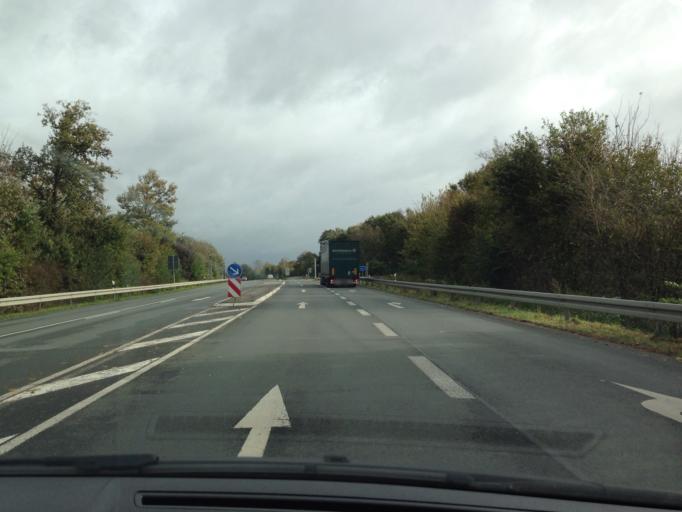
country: DE
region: North Rhine-Westphalia
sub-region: Regierungsbezirk Munster
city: Ascheberg
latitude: 51.7959
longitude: 7.6312
